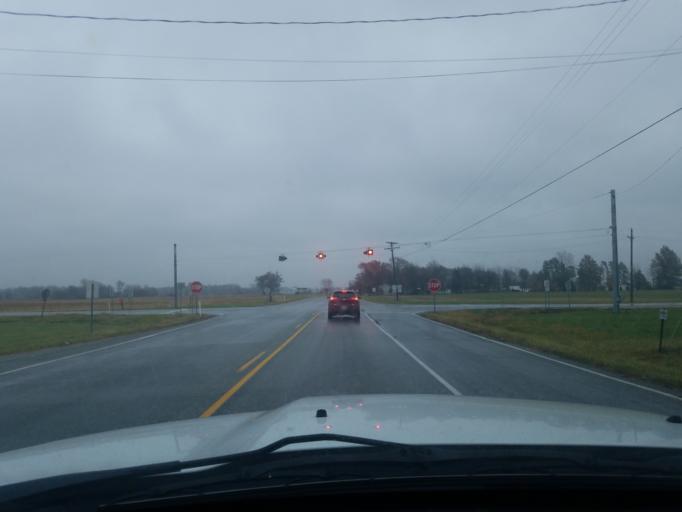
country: US
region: Indiana
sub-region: Howard County
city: Greentown
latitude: 40.4201
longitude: -86.0327
